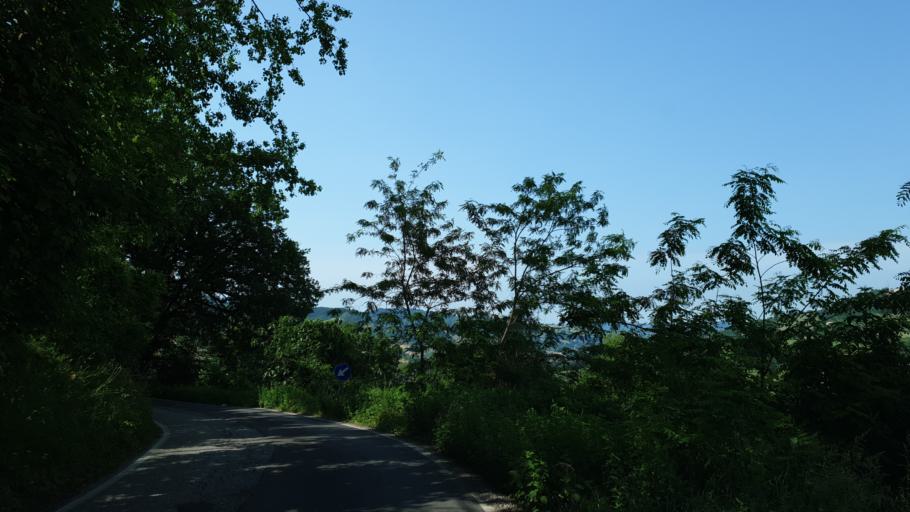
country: IT
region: Emilia-Romagna
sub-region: Forli-Cesena
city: Sarsina
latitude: 43.9124
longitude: 12.1752
